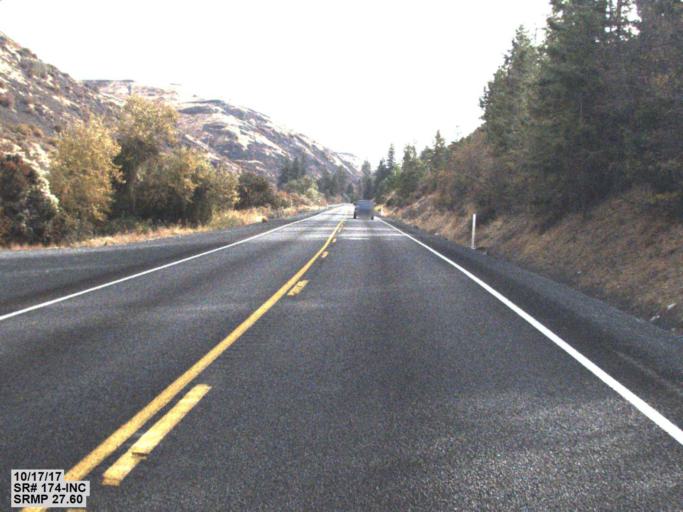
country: US
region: Washington
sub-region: Okanogan County
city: Coulee Dam
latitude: 47.9149
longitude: -118.8966
